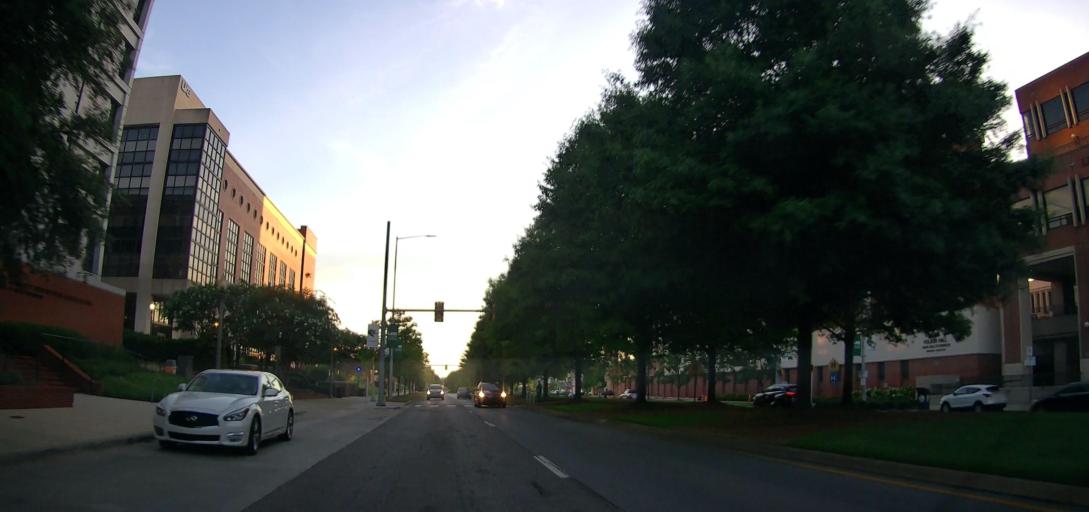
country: US
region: Alabama
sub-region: Jefferson County
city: Birmingham
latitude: 33.5027
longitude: -86.8032
